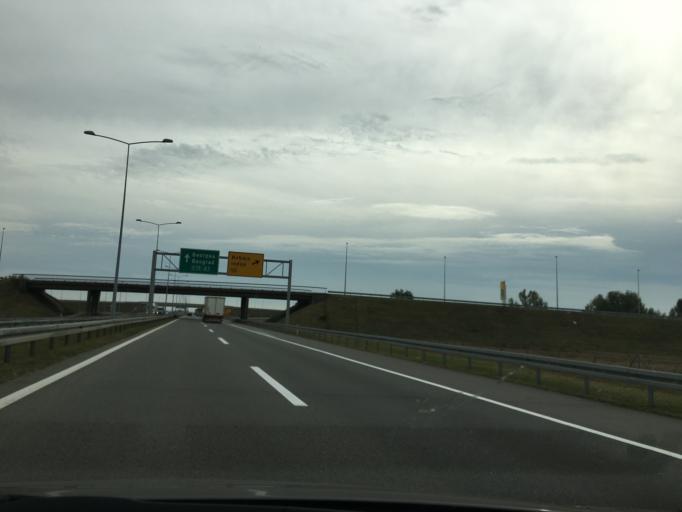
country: RS
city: Novi Karlovci
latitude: 45.0726
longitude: 20.1482
